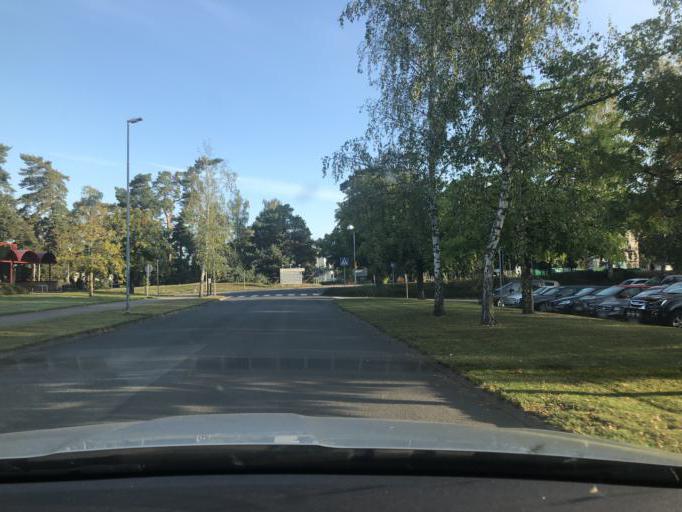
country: SE
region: Joenkoeping
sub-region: Jonkopings Kommun
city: Jonkoping
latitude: 57.7674
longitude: 14.1922
